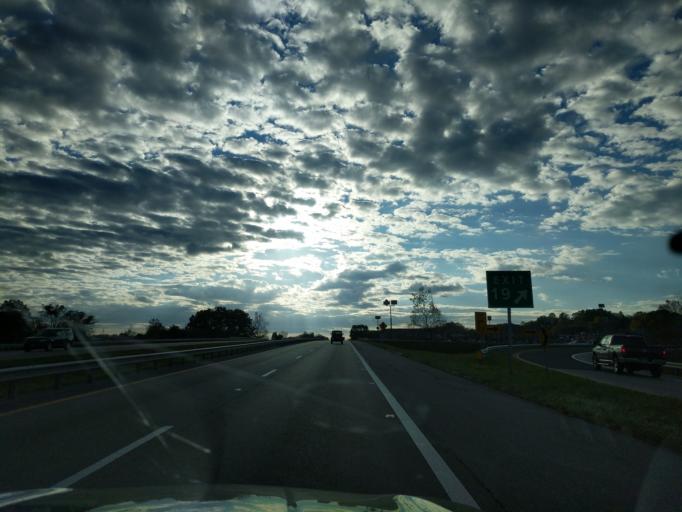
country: US
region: Virginia
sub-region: Washington County
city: Abingdon
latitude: 36.7148
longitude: -81.9311
